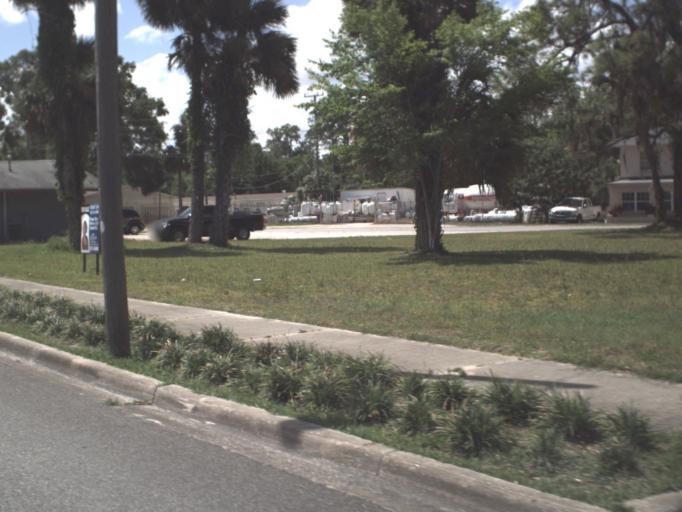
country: US
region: Florida
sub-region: Flagler County
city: Bunnell
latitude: 29.4624
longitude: -81.2532
